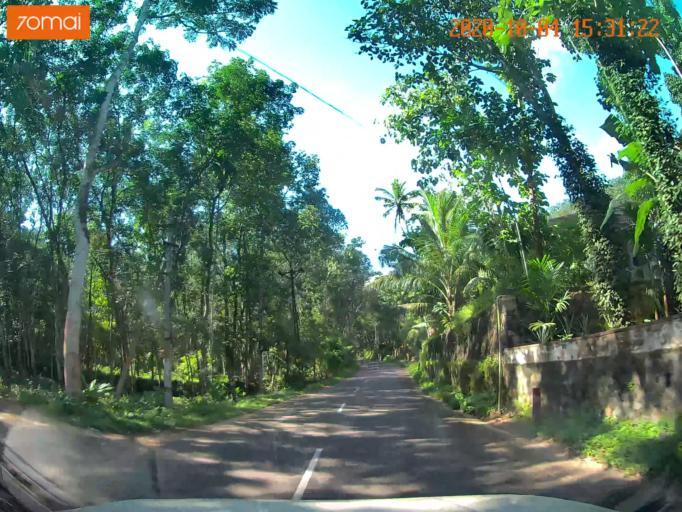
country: IN
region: Kerala
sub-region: Kottayam
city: Palackattumala
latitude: 9.7292
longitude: 76.6390
